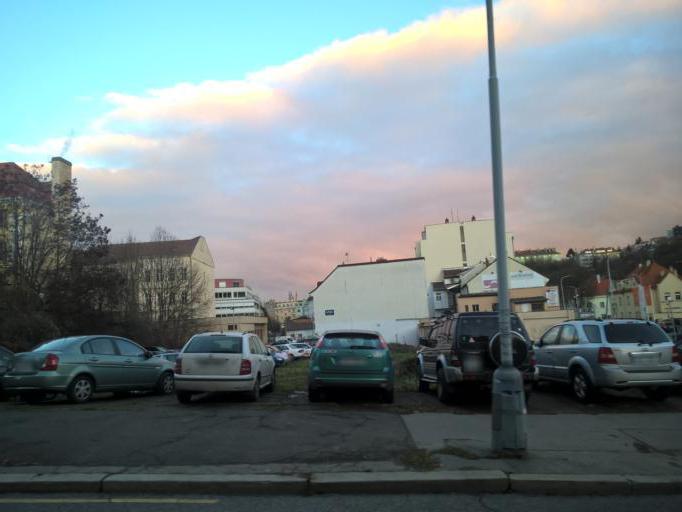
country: CZ
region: Praha
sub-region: Praha 1
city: Mala Strana
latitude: 50.0699
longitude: 14.3804
